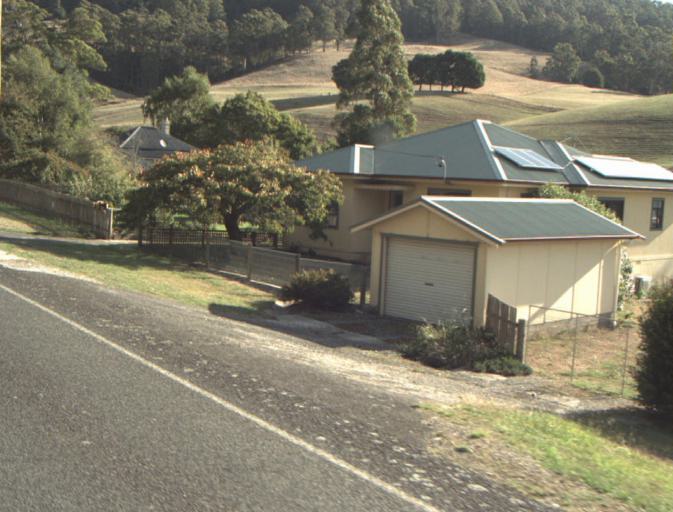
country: AU
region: Tasmania
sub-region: Launceston
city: Mayfield
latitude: -41.2656
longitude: 147.2152
